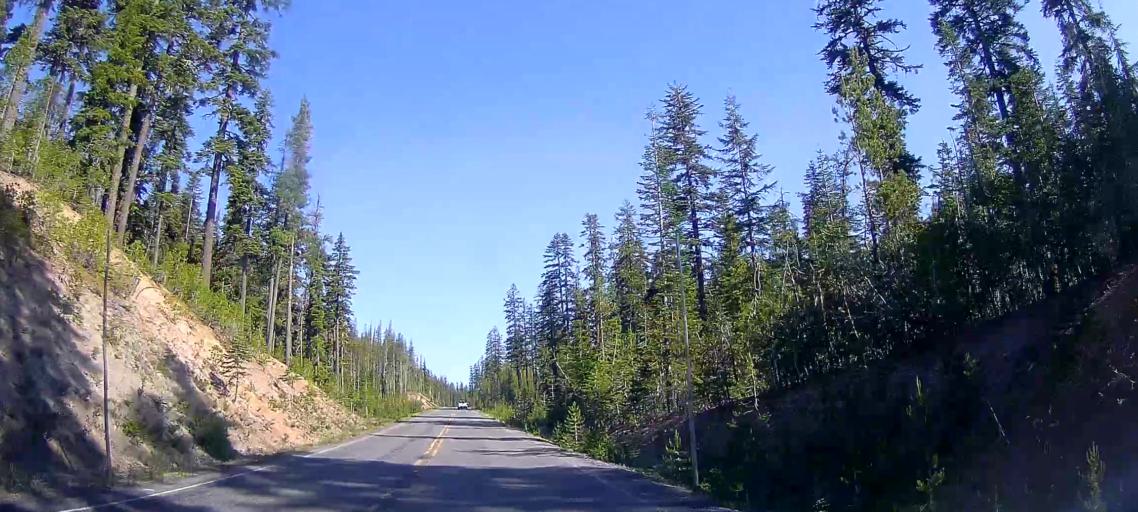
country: US
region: Oregon
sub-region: Jackson County
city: Shady Cove
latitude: 42.8485
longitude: -122.1471
